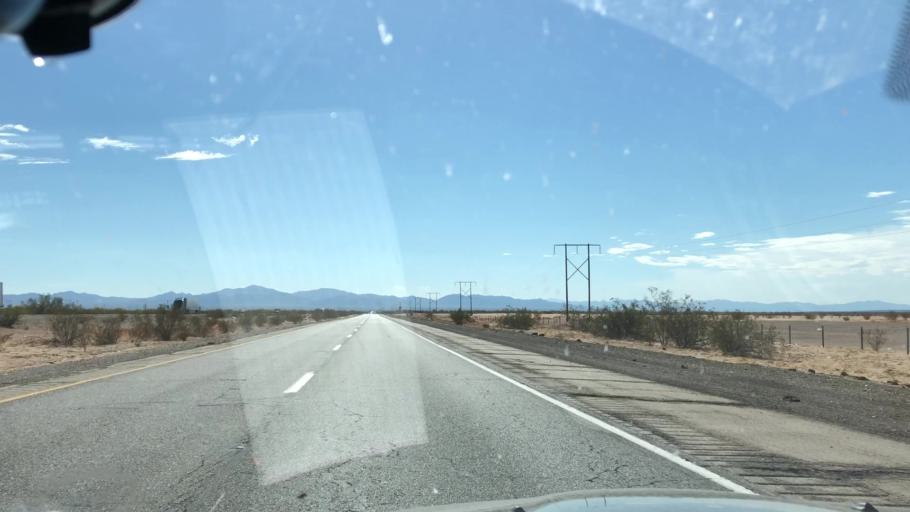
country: US
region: California
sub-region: Riverside County
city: Mesa Verde
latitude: 33.6063
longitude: -114.9518
